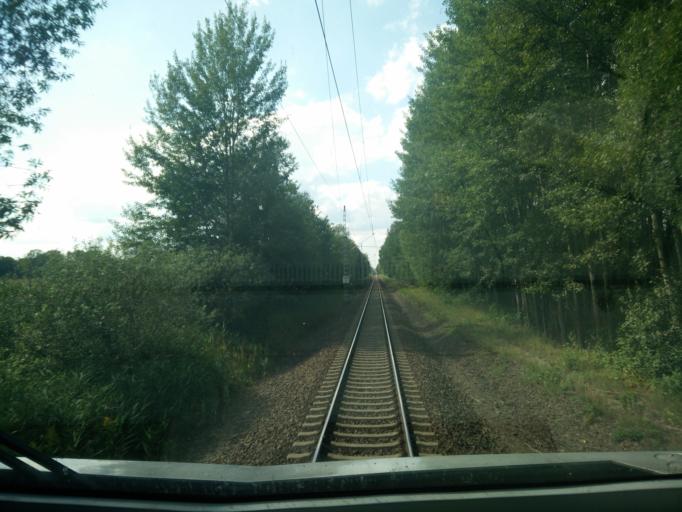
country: DE
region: Brandenburg
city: Werben
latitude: 51.7711
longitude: 14.1770
